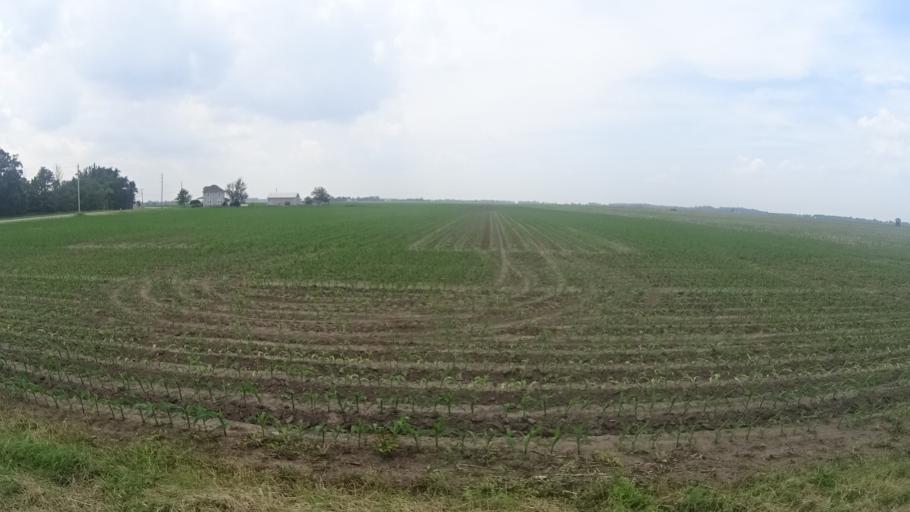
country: US
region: Ohio
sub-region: Huron County
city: Monroeville
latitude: 41.2915
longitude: -82.6718
